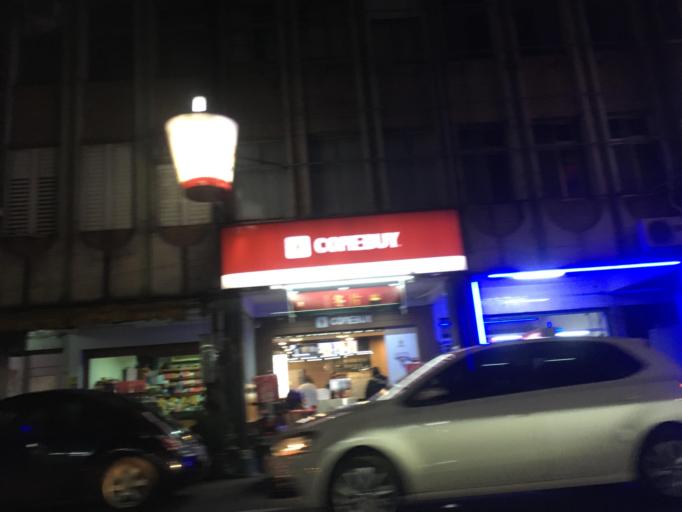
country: TW
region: Taiwan
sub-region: Yilan
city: Yilan
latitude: 24.8559
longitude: 121.8237
